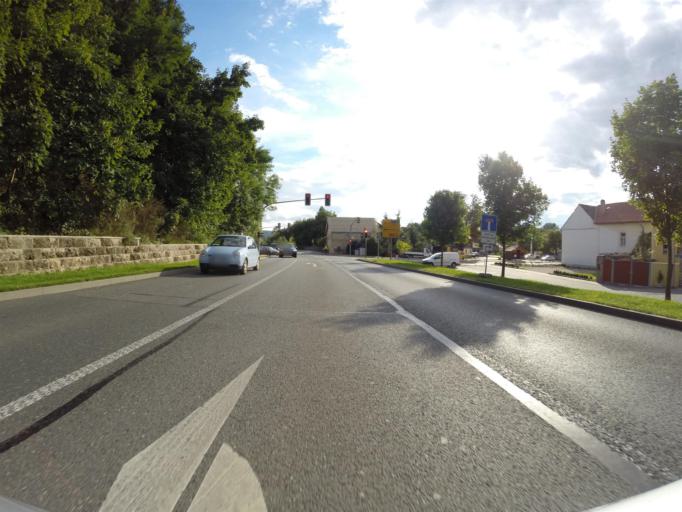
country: DE
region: Thuringia
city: Mellingen
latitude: 50.9411
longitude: 11.3977
